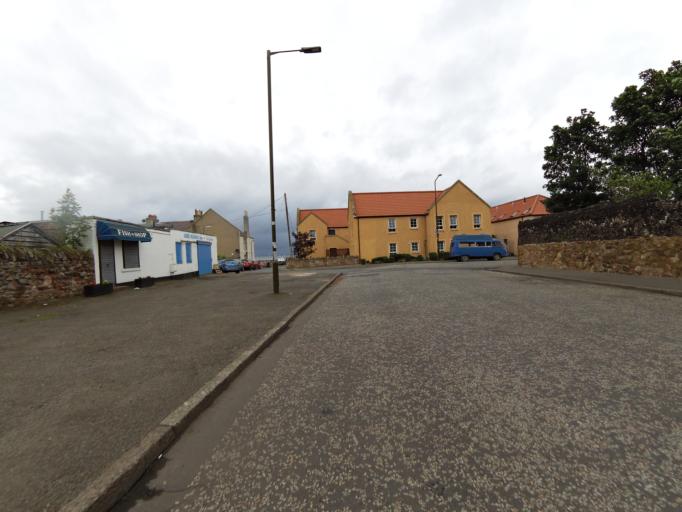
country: GB
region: Scotland
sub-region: East Lothian
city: Cockenzie
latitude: 55.9698
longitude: -2.9639
